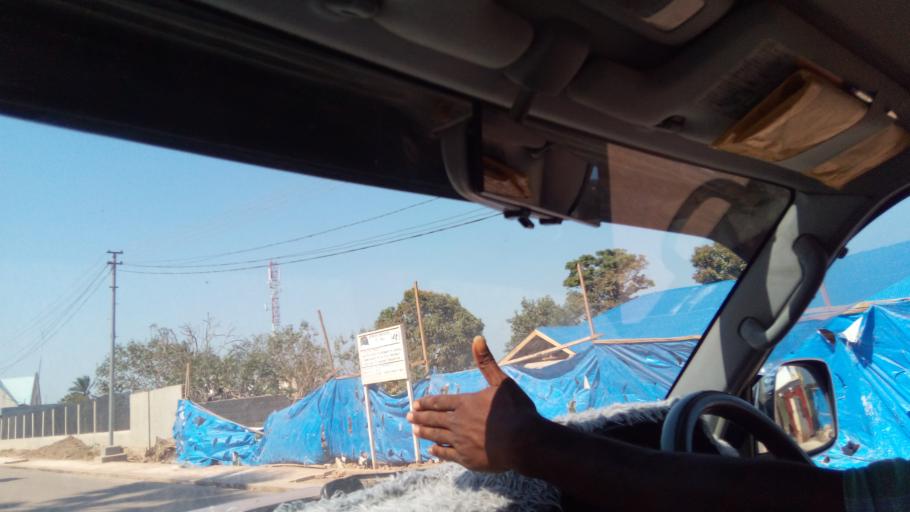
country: CD
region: Katanga
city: Kalemie
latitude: -5.9498
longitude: 29.1958
